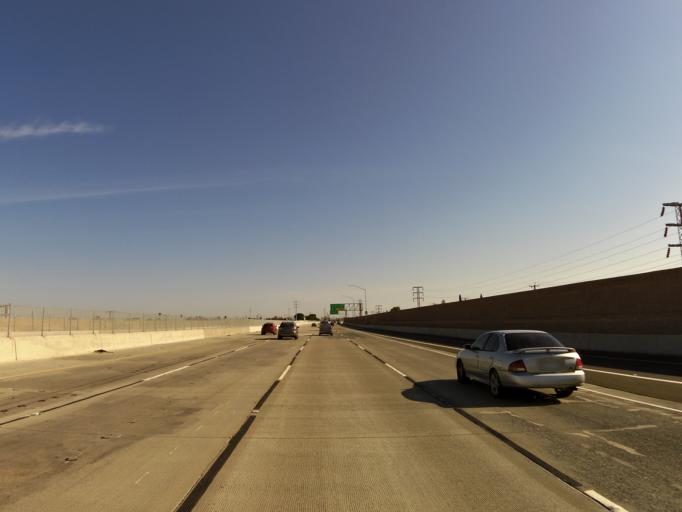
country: US
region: California
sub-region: Contra Costa County
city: Antioch
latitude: 37.9981
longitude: -121.8023
